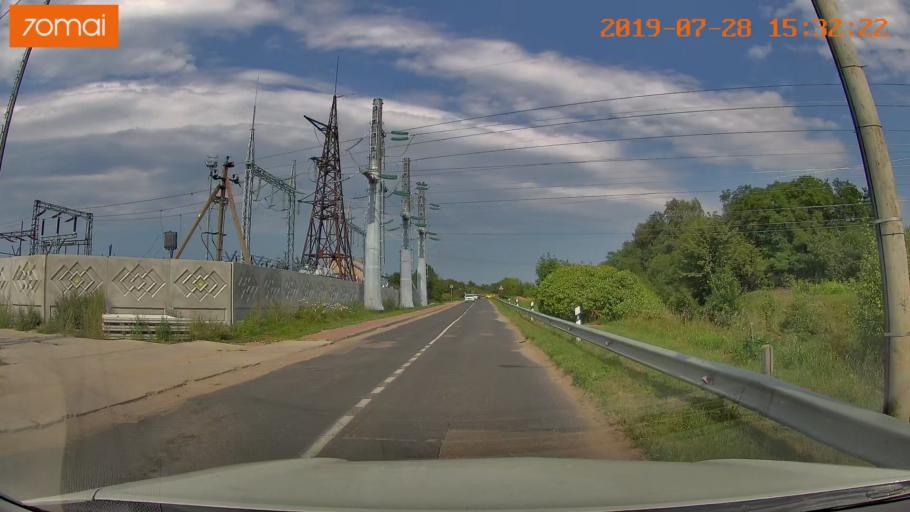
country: RU
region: Kaliningrad
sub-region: Gorod Kaliningrad
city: Yantarnyy
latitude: 54.8730
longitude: 19.9445
